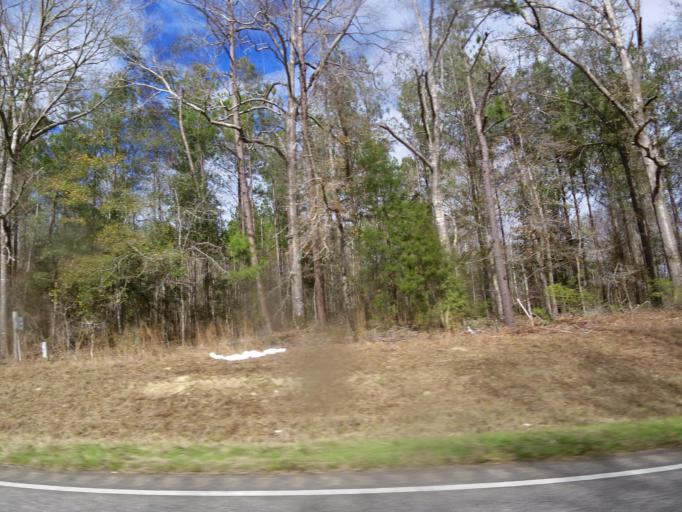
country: US
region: Alabama
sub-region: Barbour County
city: Eufaula
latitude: 31.9904
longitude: -85.2632
